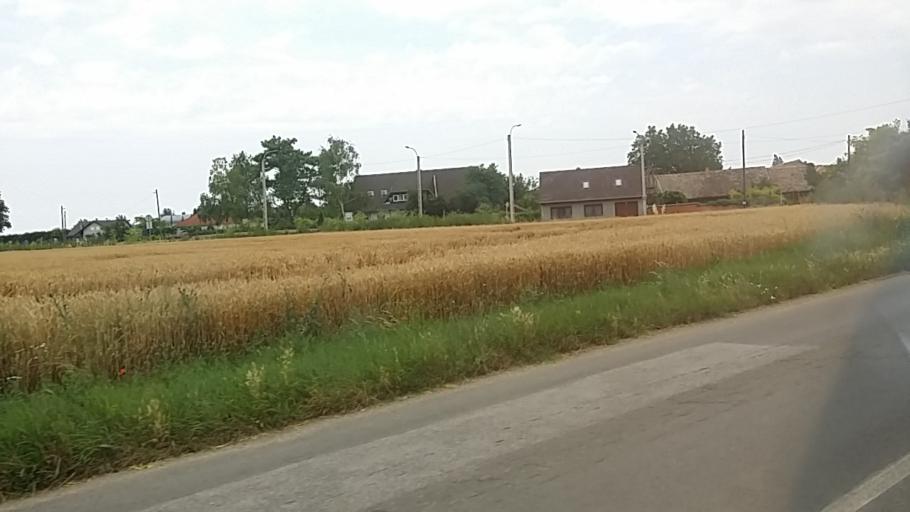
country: HU
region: Baranya
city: Boly
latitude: 45.9860
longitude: 18.5350
